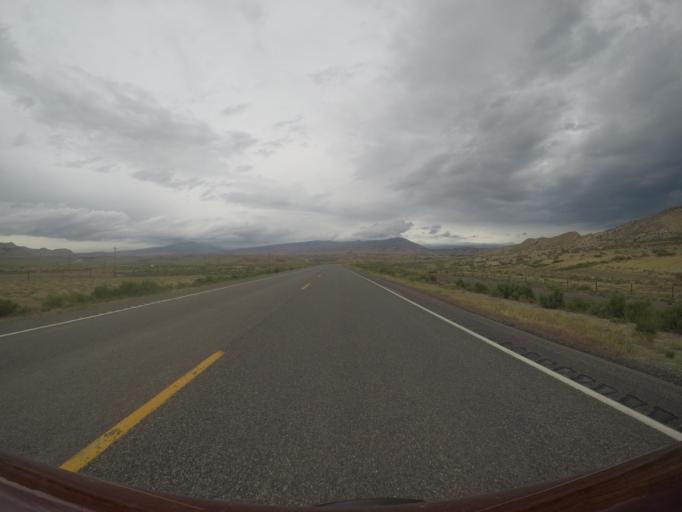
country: US
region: Wyoming
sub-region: Big Horn County
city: Lovell
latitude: 44.9457
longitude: -108.2969
